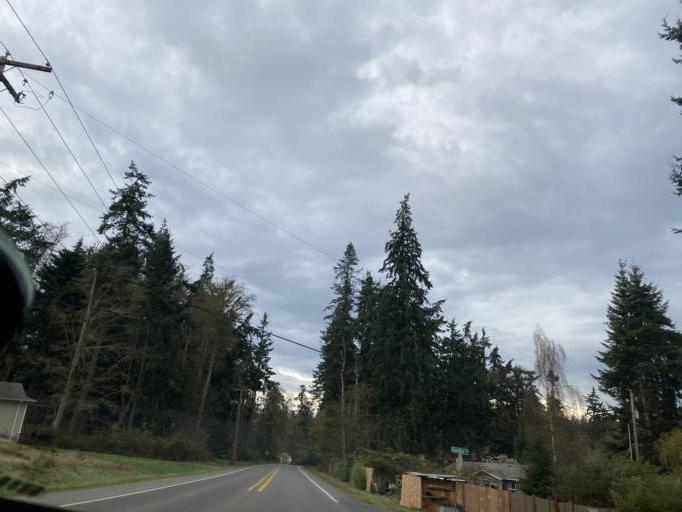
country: US
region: Washington
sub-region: Island County
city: Freeland
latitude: 48.0029
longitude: -122.5323
